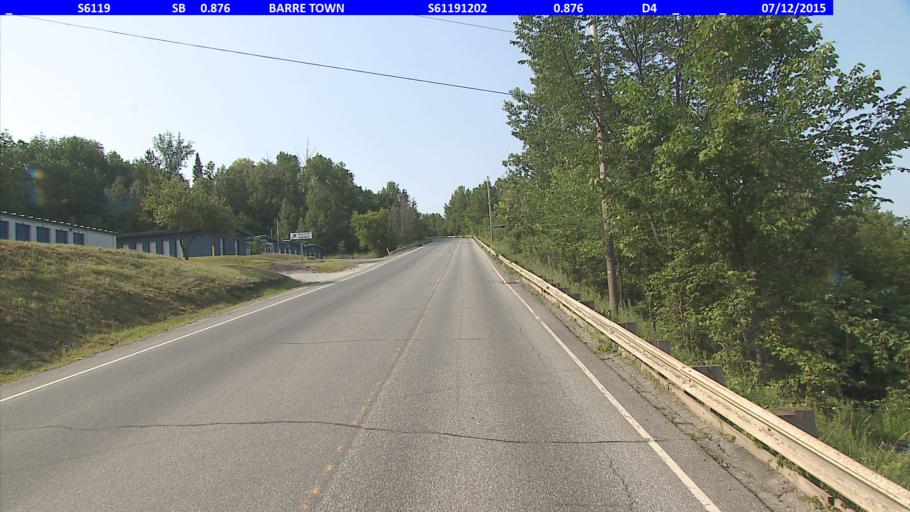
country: US
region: Vermont
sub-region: Washington County
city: South Barre
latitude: 44.1796
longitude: -72.4957
